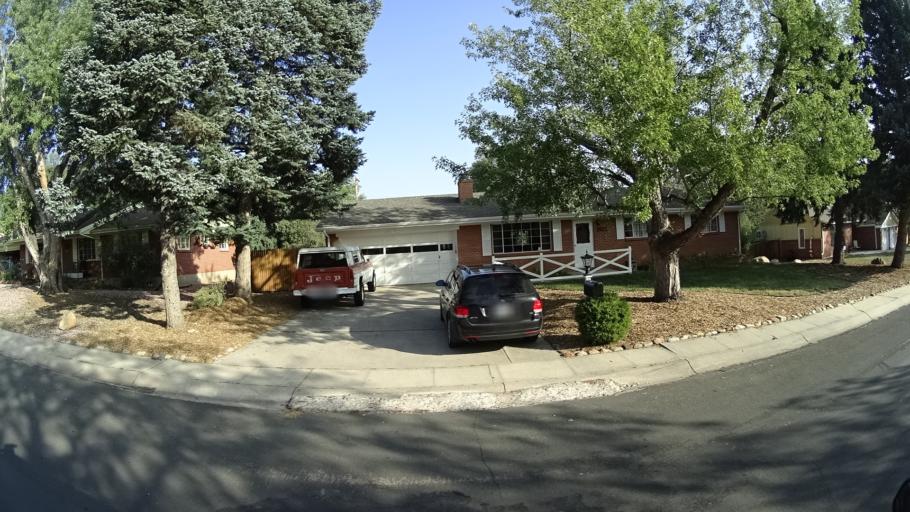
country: US
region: Colorado
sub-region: El Paso County
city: Colorado Springs
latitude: 38.8141
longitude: -104.8571
